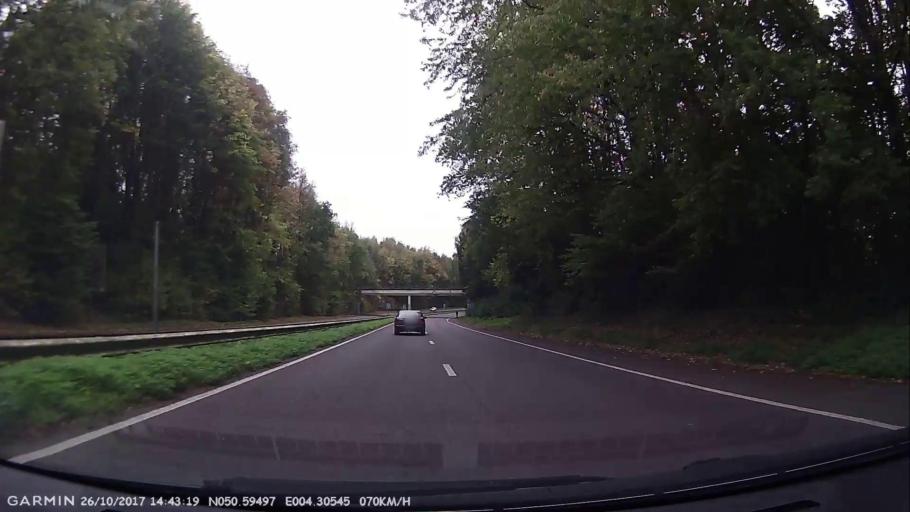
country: BE
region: Wallonia
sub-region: Province du Brabant Wallon
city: Nivelles
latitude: 50.5951
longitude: 4.3054
